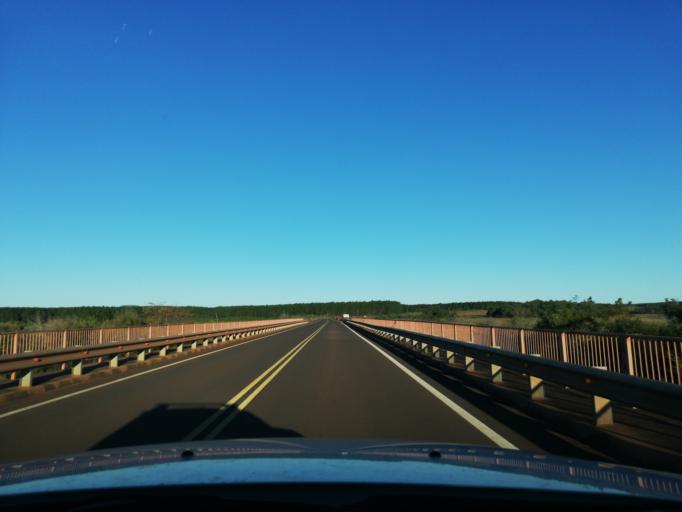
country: AR
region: Misiones
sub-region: Departamento de Candelaria
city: Candelaria
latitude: -27.4897
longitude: -55.7410
